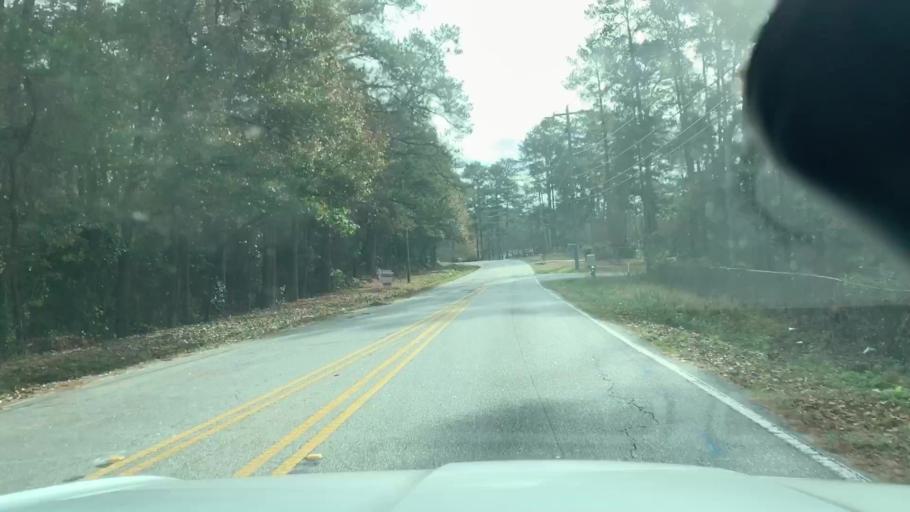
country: US
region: South Carolina
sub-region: Richland County
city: Woodfield
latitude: 34.0828
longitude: -80.9320
